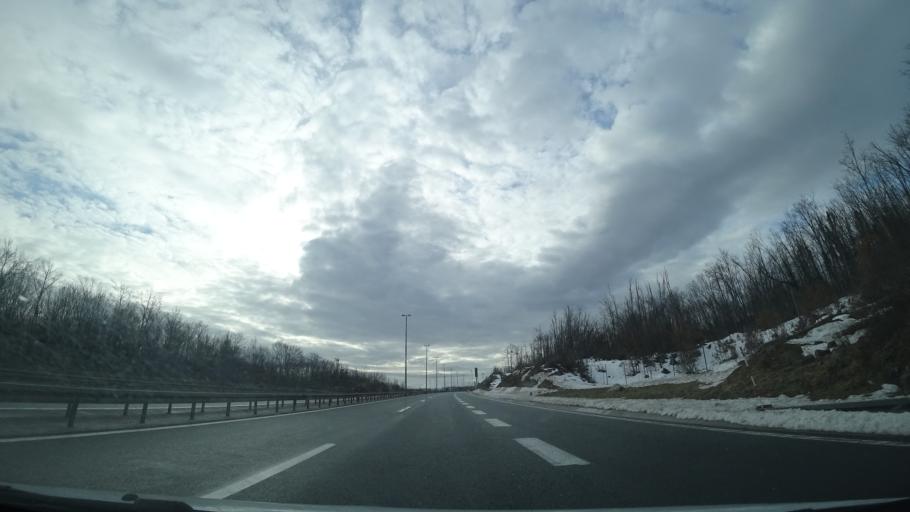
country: HR
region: Licko-Senjska
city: Otocac
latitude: 44.7545
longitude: 15.3707
